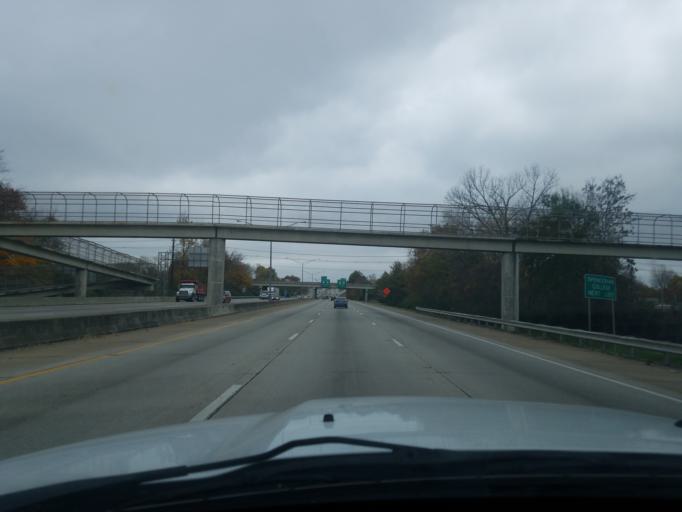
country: US
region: Kentucky
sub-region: Jefferson County
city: Shively
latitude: 38.1866
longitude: -85.7982
